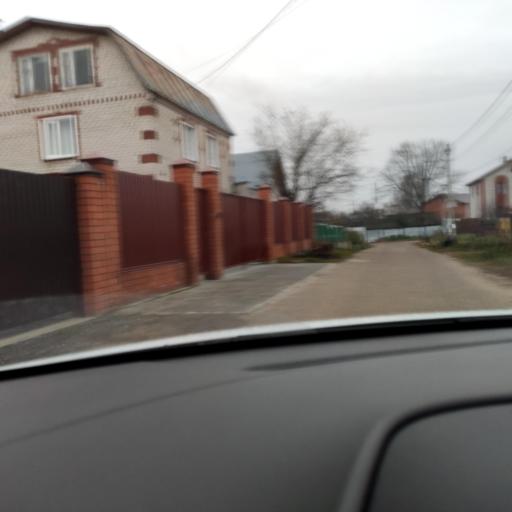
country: RU
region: Tatarstan
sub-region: Gorod Kazan'
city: Kazan
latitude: 55.8630
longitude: 49.0611
